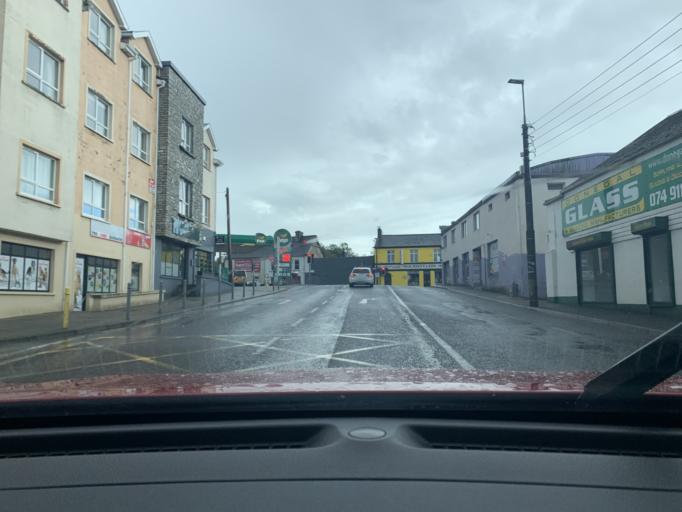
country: IE
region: Ulster
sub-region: County Donegal
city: Ballybofey
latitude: 54.8055
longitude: -7.7684
